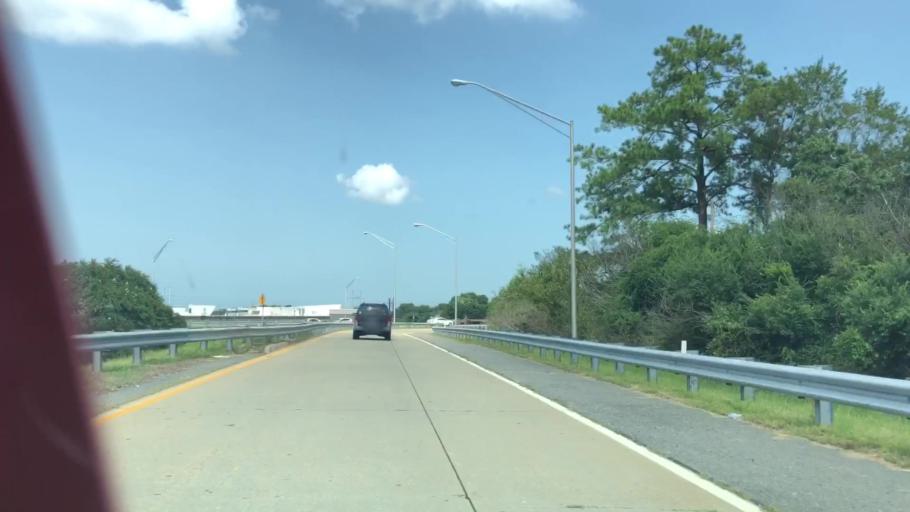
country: US
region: Virginia
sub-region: City of Virginia Beach
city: Virginia Beach
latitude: 36.8451
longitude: -76.0187
